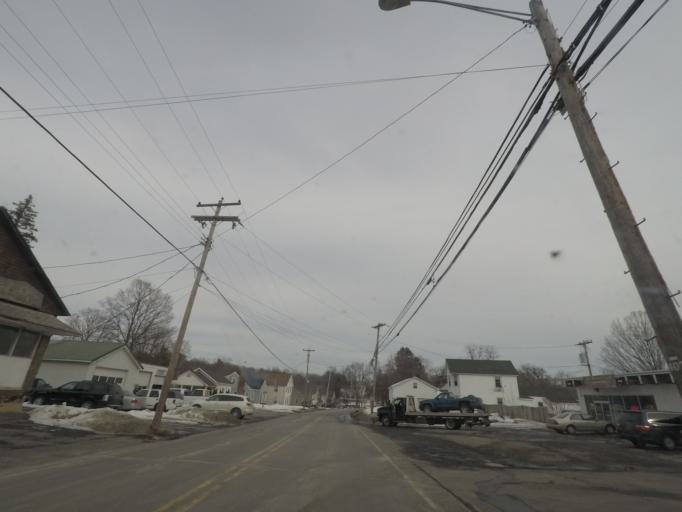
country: US
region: New York
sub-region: Albany County
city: Voorheesville
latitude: 42.5759
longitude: -73.9635
